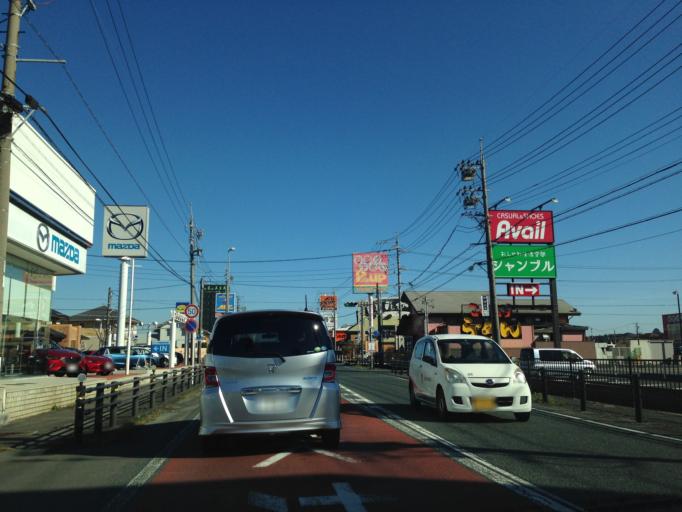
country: JP
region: Shizuoka
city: Kakegawa
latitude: 34.7716
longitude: 137.9804
